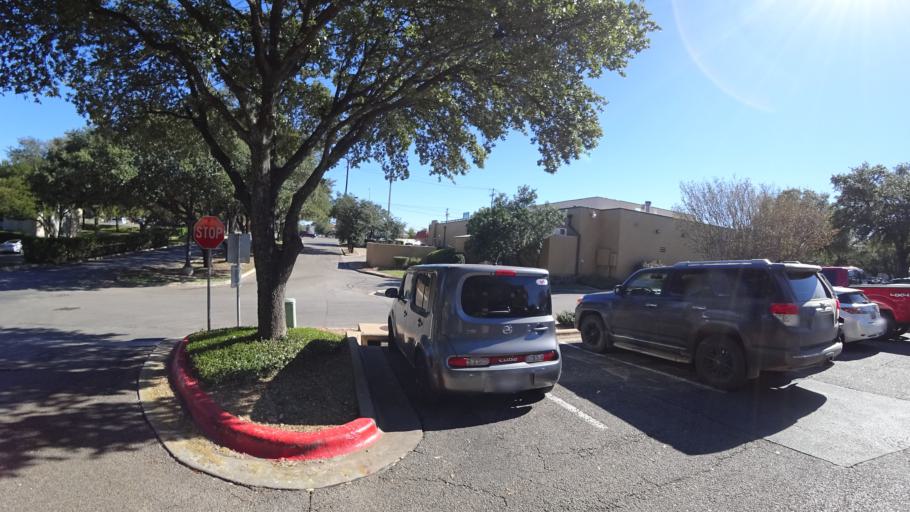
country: US
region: Texas
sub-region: Travis County
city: Rollingwood
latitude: 30.2376
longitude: -97.7923
